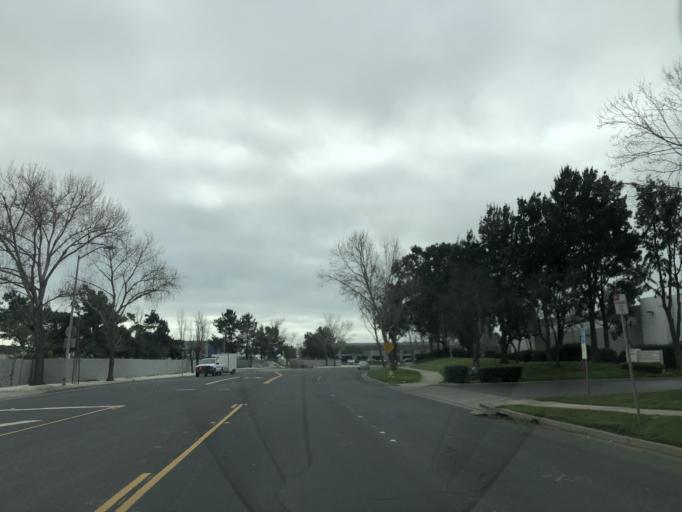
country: US
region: California
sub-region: Alameda County
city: Newark
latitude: 37.5233
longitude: -122.0303
